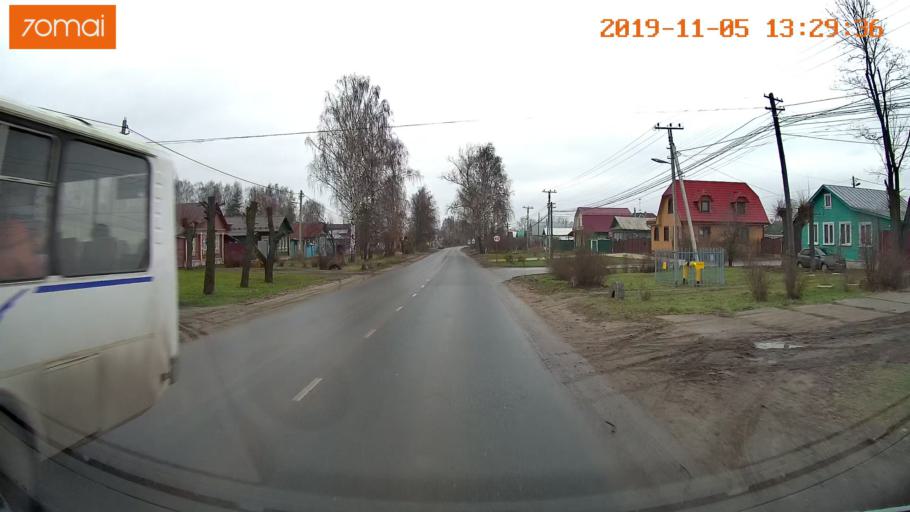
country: RU
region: Ivanovo
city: Shuya
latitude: 56.8618
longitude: 41.3974
